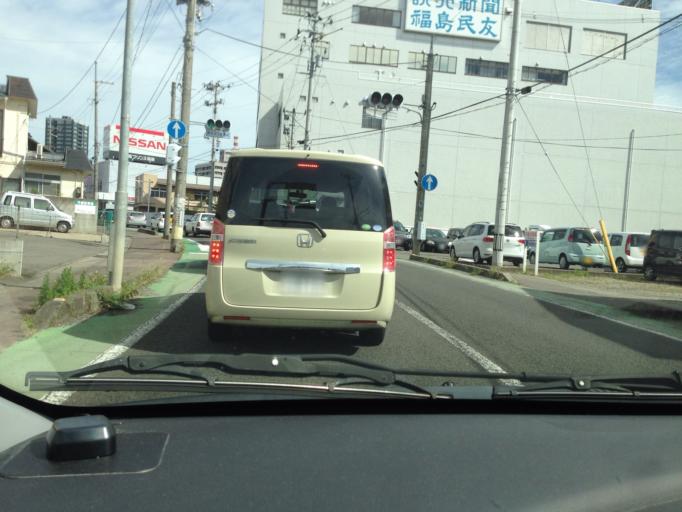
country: JP
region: Fukushima
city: Fukushima-shi
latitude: 37.7464
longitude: 140.4642
